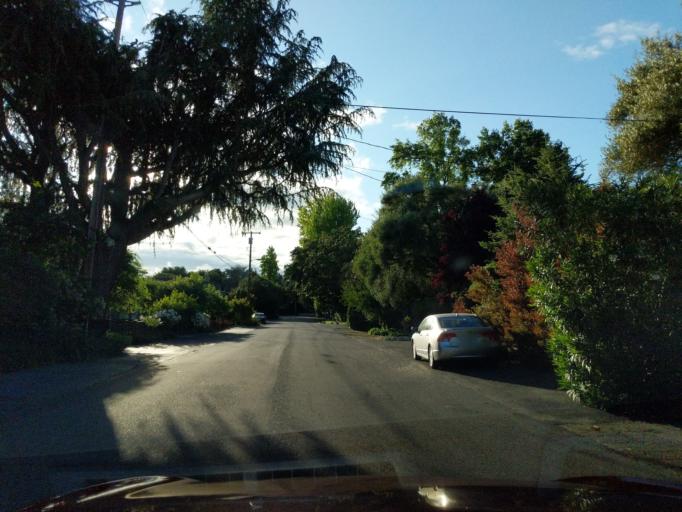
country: US
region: California
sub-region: San Mateo County
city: Menlo Park
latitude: 37.4389
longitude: -122.1845
